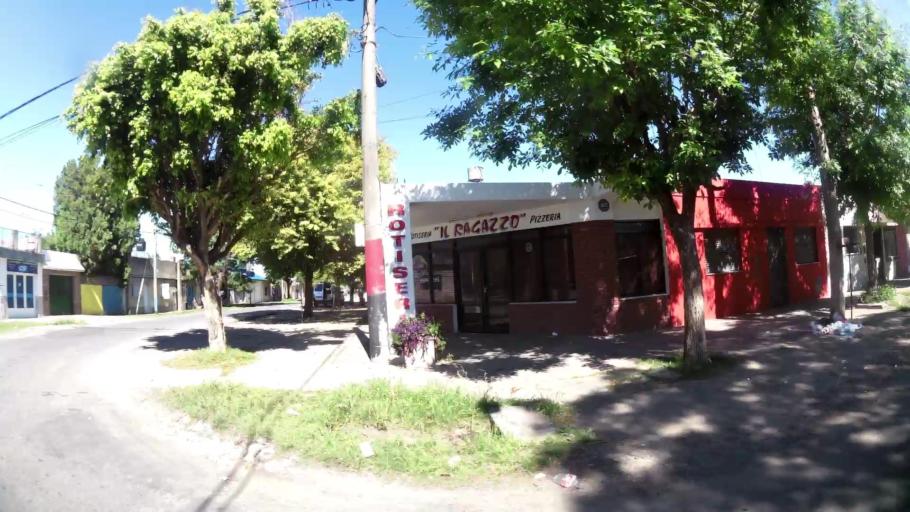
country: AR
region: Santa Fe
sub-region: Departamento de Rosario
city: Rosario
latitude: -32.9647
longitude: -60.6964
